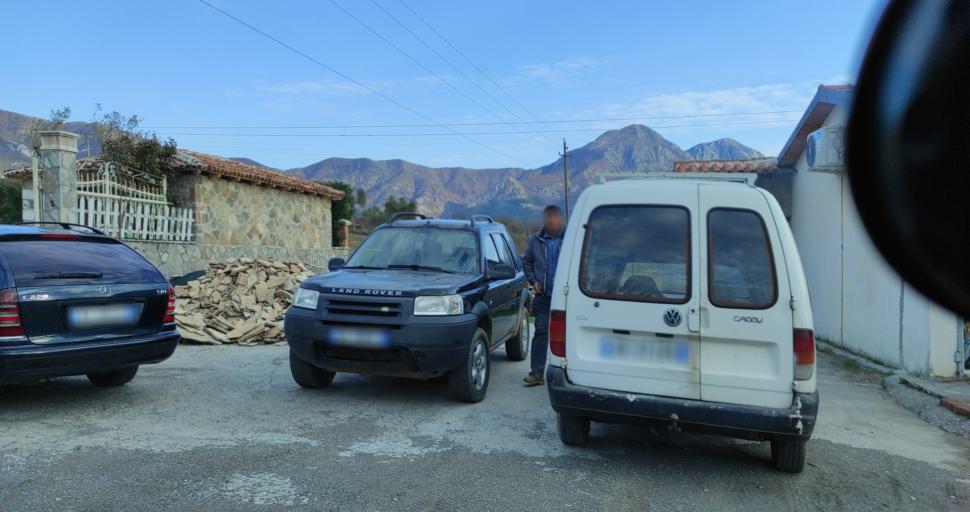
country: AL
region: Lezhe
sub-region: Rrethi i Lezhes
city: Kallmeti i Madh
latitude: 41.8822
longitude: 19.6798
